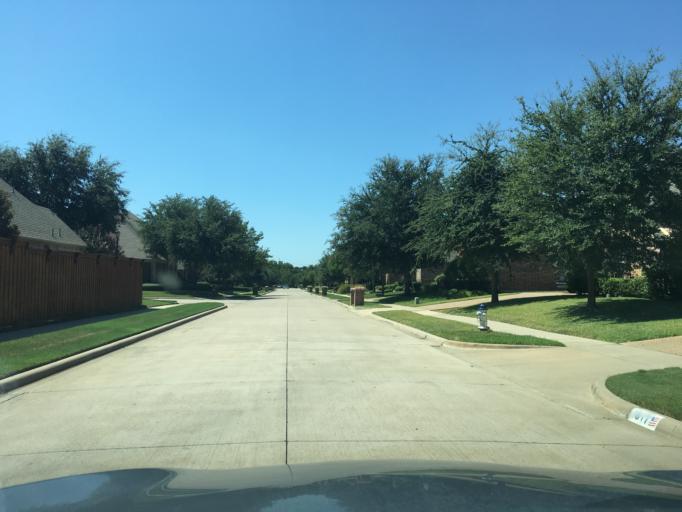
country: US
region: Texas
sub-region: Dallas County
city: Sachse
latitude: 32.9680
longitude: -96.6161
